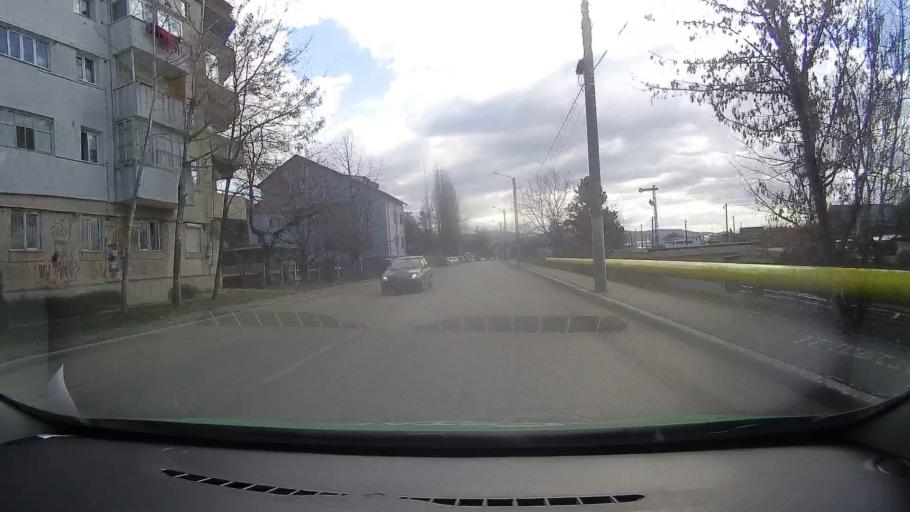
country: RO
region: Dambovita
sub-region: Oras Pucioasa
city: Pucioasa
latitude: 45.0775
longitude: 25.4299
